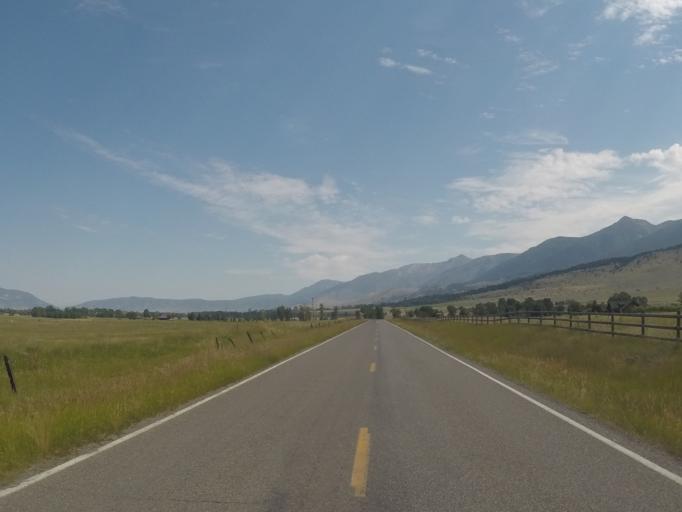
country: US
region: Montana
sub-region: Park County
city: Livingston
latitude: 45.4294
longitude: -110.6175
